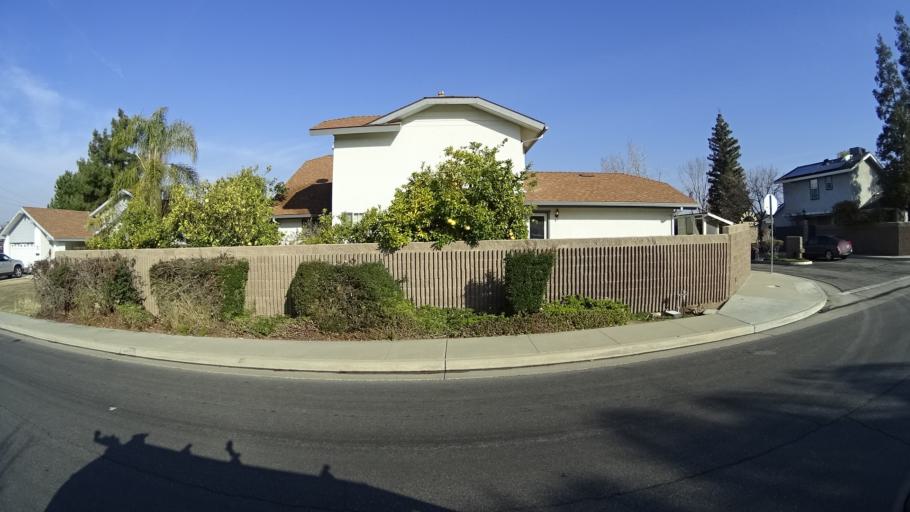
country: US
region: California
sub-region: Kern County
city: Oildale
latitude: 35.4053
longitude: -118.9275
